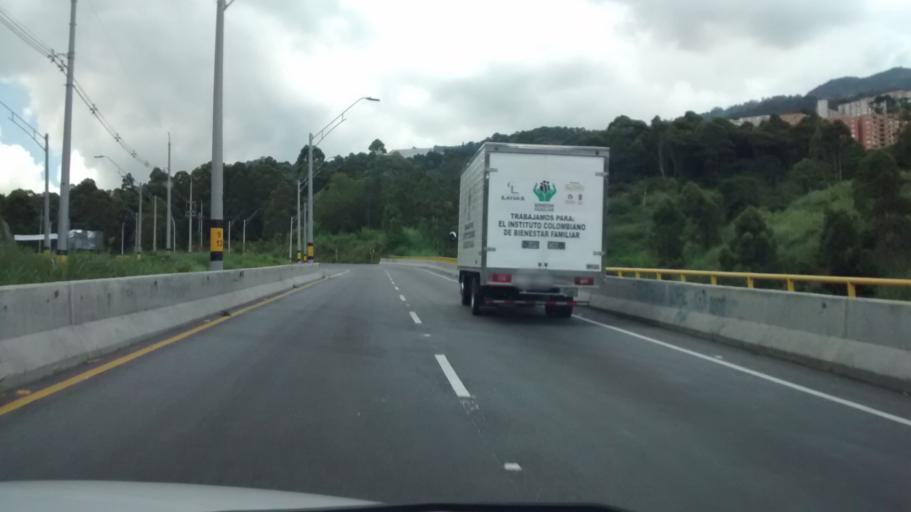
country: CO
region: Antioquia
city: Medellin
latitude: 6.2738
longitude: -75.6211
